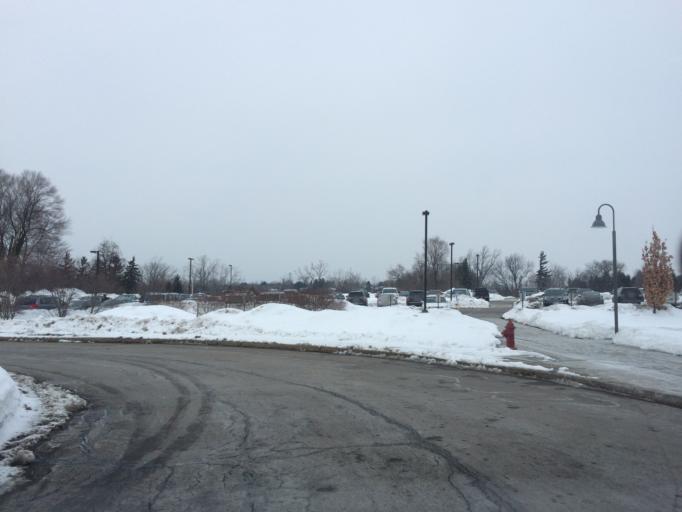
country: US
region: New York
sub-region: Monroe County
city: Fairport
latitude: 43.0834
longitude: -77.4307
